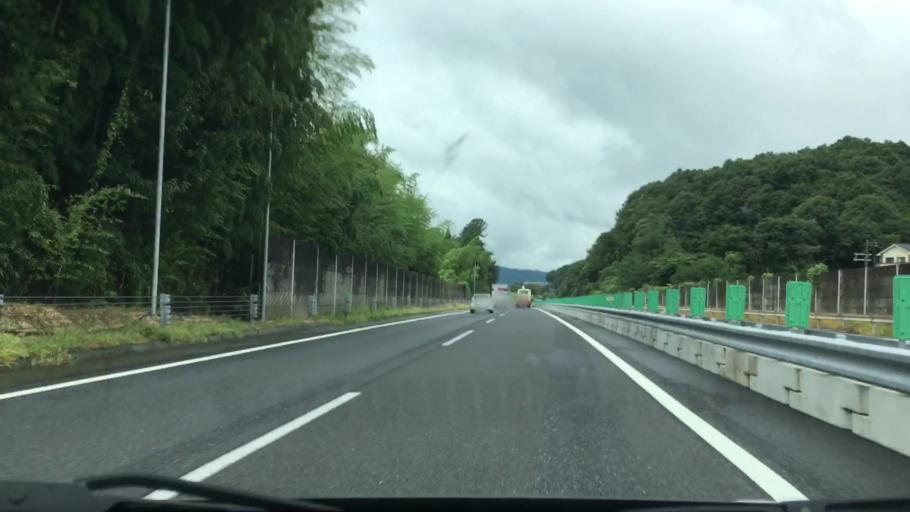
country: JP
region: Hyogo
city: Yamazakicho-nakabirose
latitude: 34.9902
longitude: 134.5902
